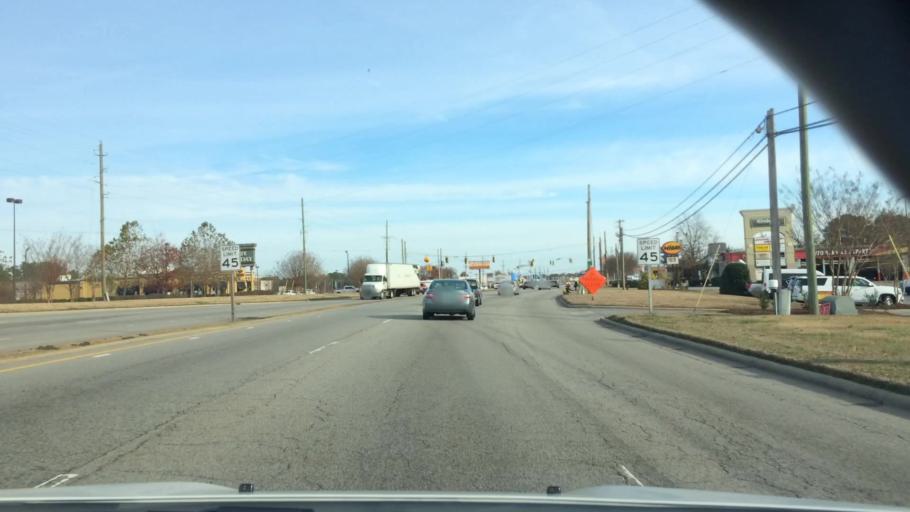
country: US
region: North Carolina
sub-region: Pitt County
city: Summerfield
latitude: 35.5663
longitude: -77.4039
